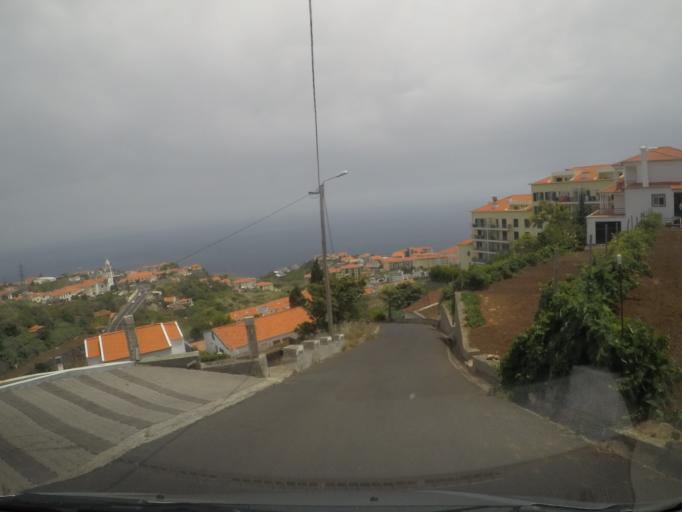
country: PT
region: Madeira
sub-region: Santa Cruz
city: Camacha
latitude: 32.6602
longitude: -16.8302
